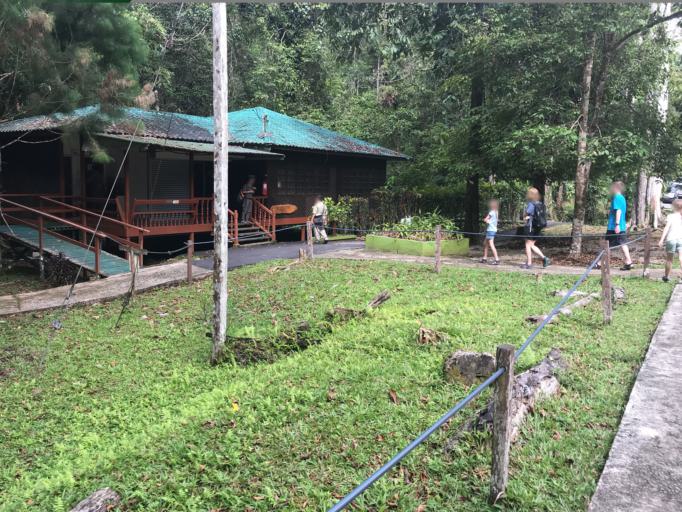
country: MY
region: Sarawak
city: Kuching
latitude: 1.4018
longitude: 110.3146
